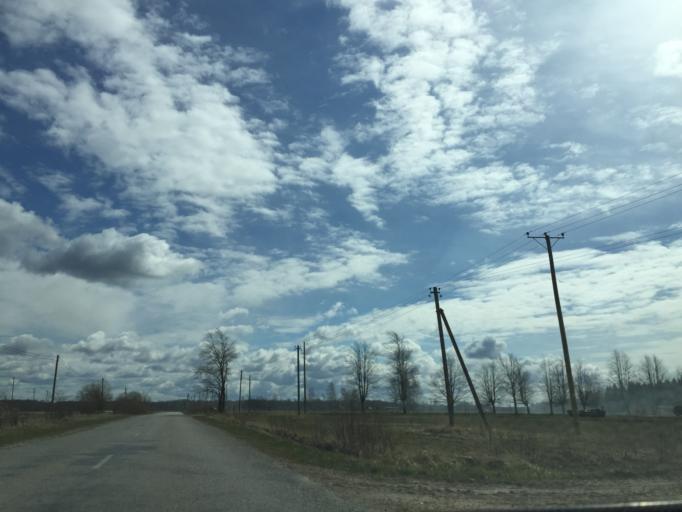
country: LV
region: Salacgrivas
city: Salacgriva
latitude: 57.7454
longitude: 24.3901
